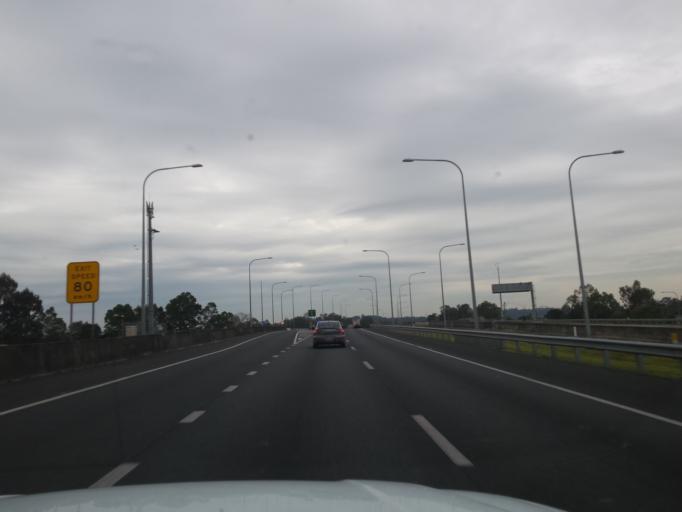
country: AU
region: Queensland
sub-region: Logan
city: Slacks Creek
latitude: -27.6651
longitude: 153.1377
